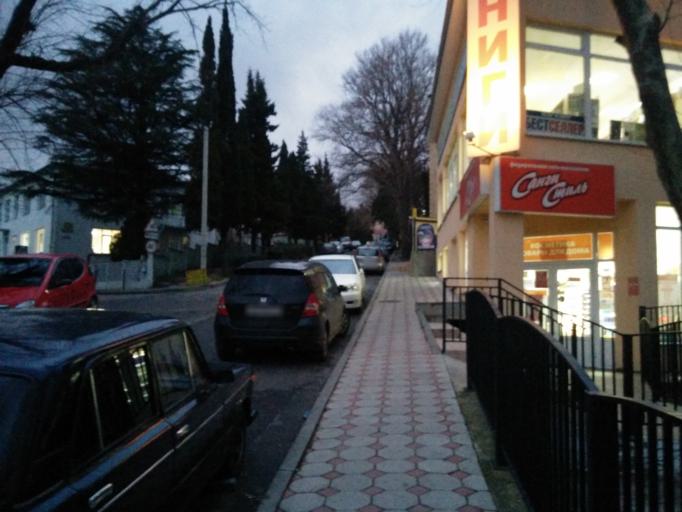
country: RU
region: Krasnodarskiy
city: Tuapse
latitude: 44.0990
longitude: 39.0777
